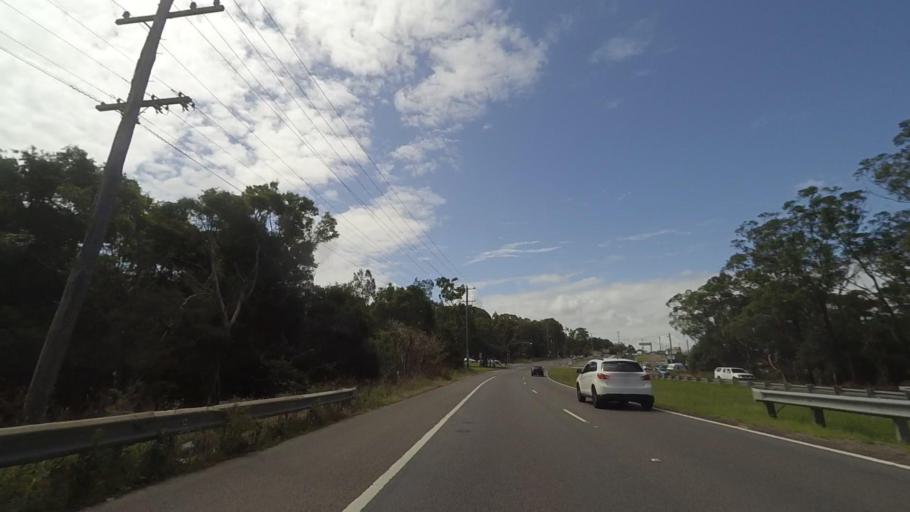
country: AU
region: New South Wales
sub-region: Lake Macquarie Shire
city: Windale
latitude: -33.0005
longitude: 151.6857
